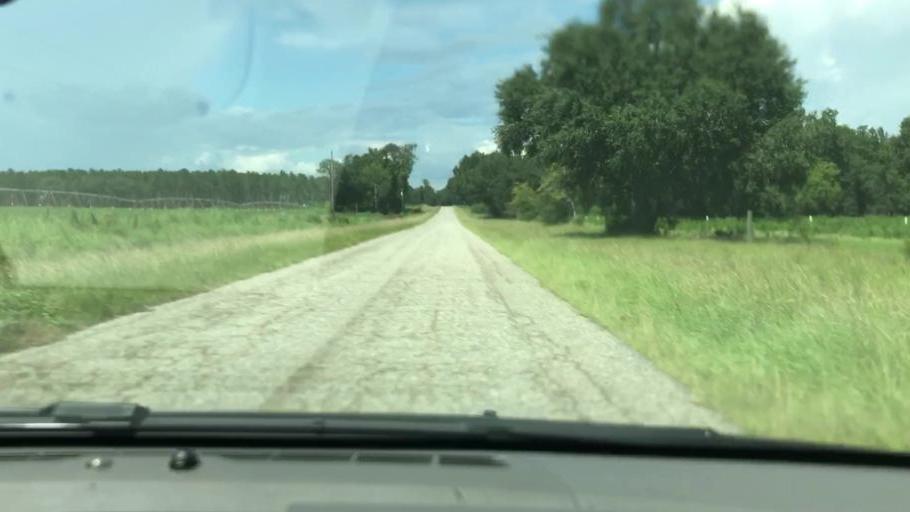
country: US
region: Georgia
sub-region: Early County
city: Blakely
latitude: 31.2155
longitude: -85.0032
